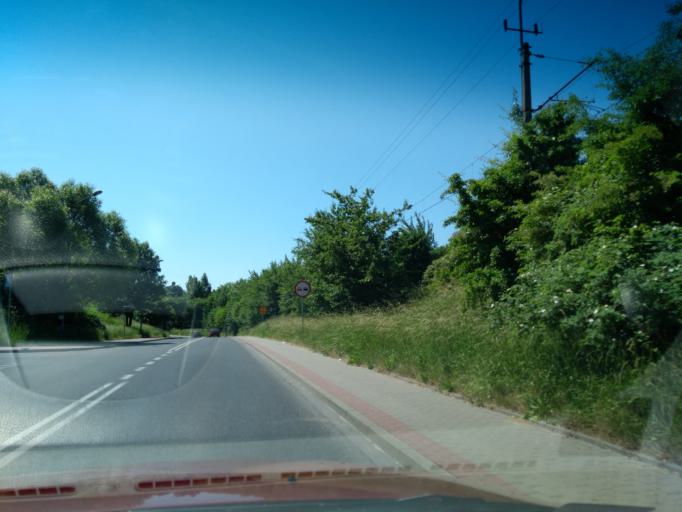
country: PL
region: West Pomeranian Voivodeship
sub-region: Koszalin
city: Koszalin
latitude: 54.2038
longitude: 16.1739
